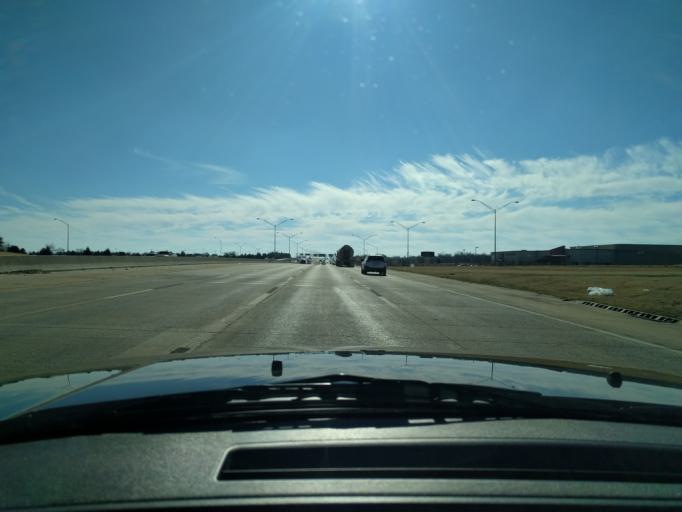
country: US
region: Oklahoma
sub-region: Oklahoma County
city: Nichols Hills
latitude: 35.5640
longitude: -97.5141
